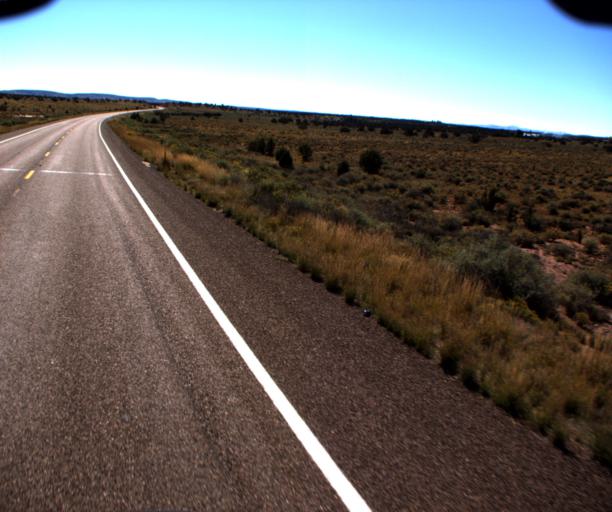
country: US
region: Arizona
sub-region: Apache County
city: Saint Johns
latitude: 34.6143
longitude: -109.6539
